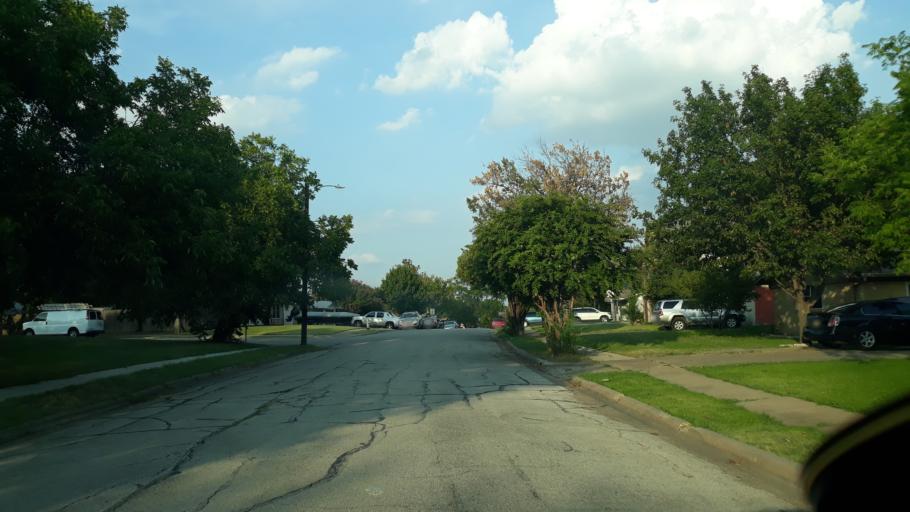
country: US
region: Texas
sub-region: Dallas County
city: Irving
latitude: 32.8474
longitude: -96.9831
